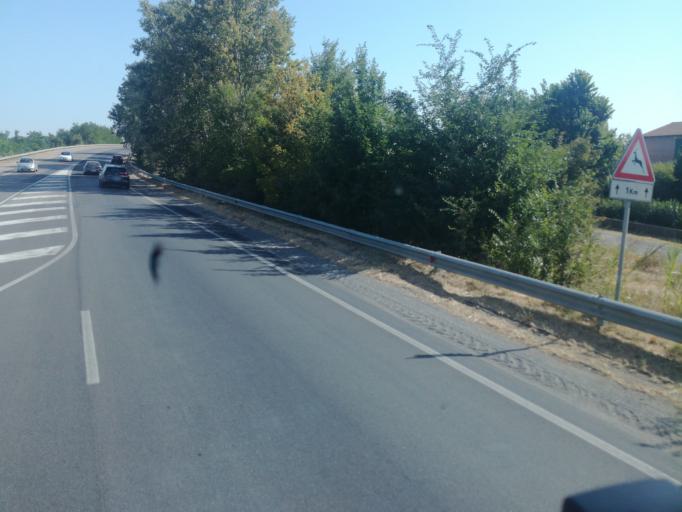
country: IT
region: Emilia-Romagna
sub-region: Provincia di Bologna
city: Castel San Pietro Terme
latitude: 44.4079
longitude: 11.5885
